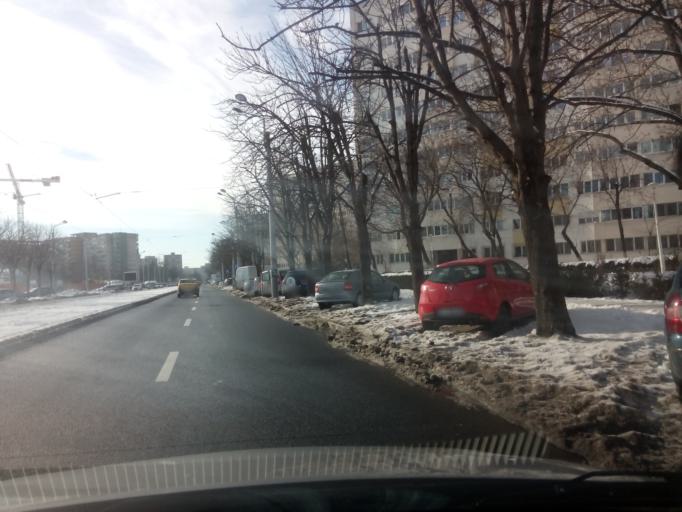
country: RO
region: Ilfov
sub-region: Comuna Fundeni-Dobroesti
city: Fundeni
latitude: 44.4224
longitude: 26.1496
